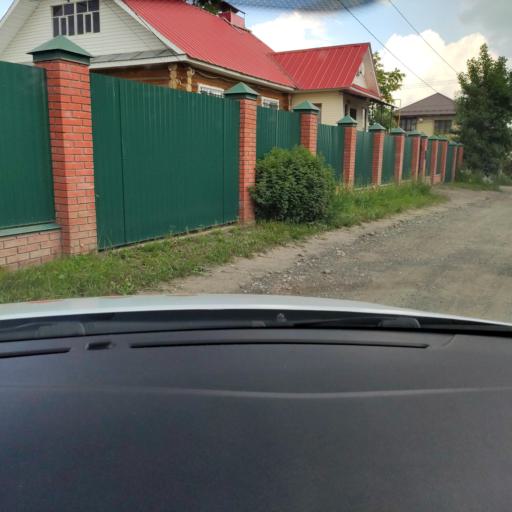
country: RU
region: Tatarstan
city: Stolbishchi
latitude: 55.7498
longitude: 49.2850
